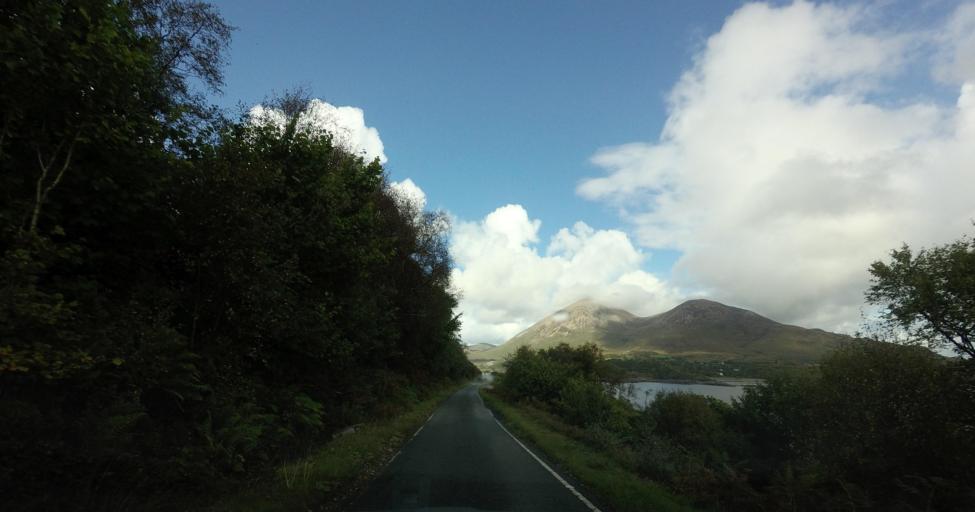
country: GB
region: Scotland
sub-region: Highland
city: Portree
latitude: 57.1971
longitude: -6.0280
